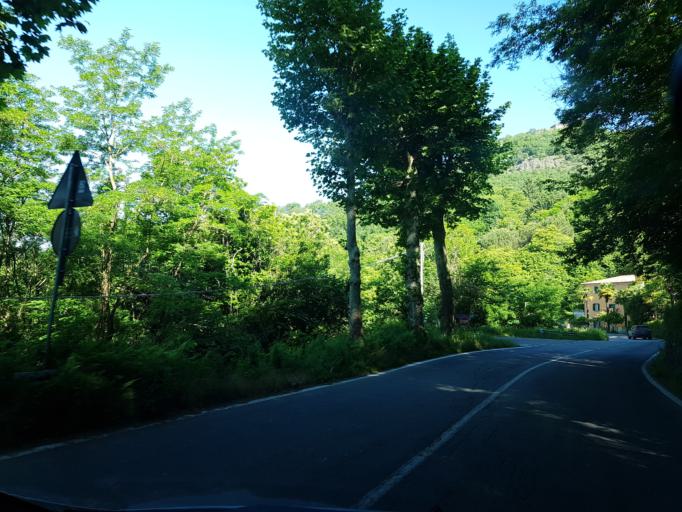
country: IT
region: Tuscany
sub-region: Provincia di Lucca
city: San Romano
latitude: 44.1735
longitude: 10.3368
